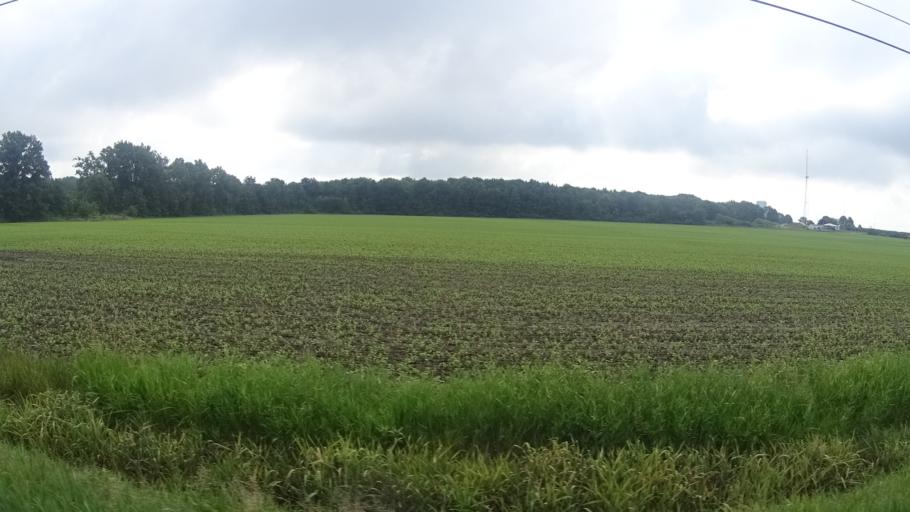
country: US
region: Ohio
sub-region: Erie County
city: Huron
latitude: 41.3084
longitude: -82.4930
